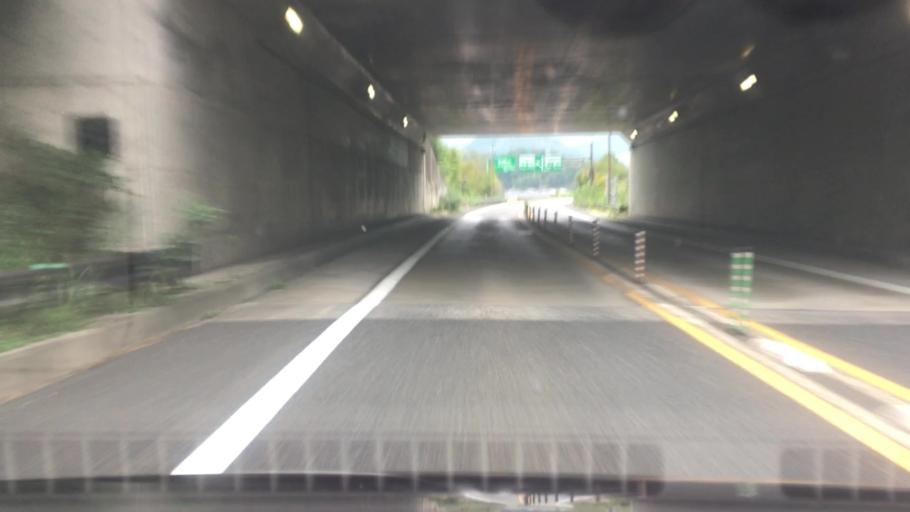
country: JP
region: Hyogo
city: Toyooka
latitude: 35.3099
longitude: 134.8616
